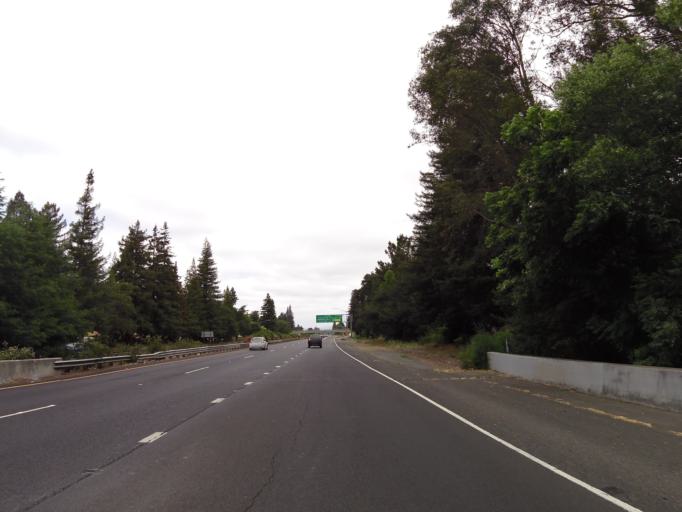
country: US
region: California
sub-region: Napa County
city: Napa
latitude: 38.3013
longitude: -122.3030
